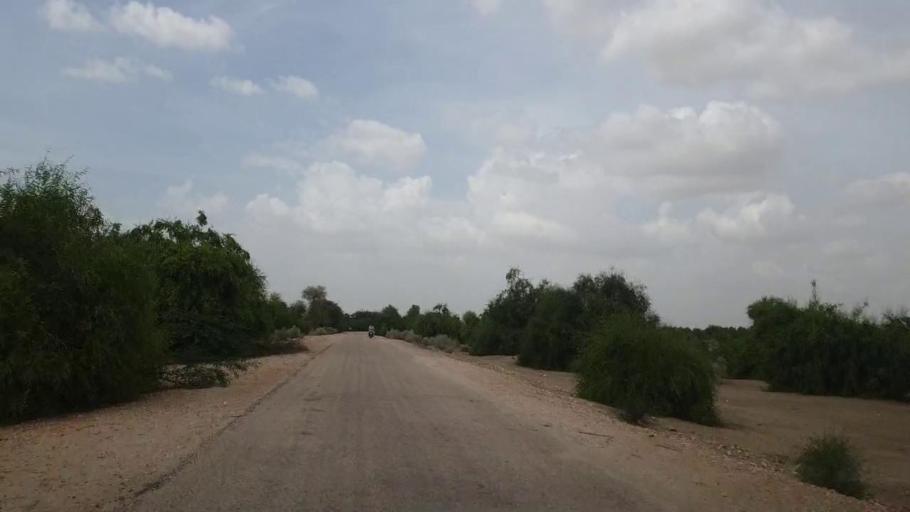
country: PK
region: Sindh
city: Kot Diji
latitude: 27.2193
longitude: 69.0840
